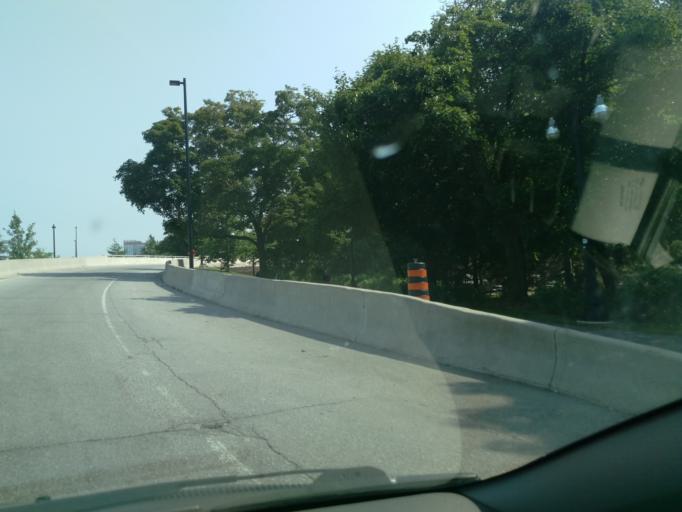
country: CA
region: Ontario
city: Ottawa
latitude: 45.4378
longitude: -75.6949
